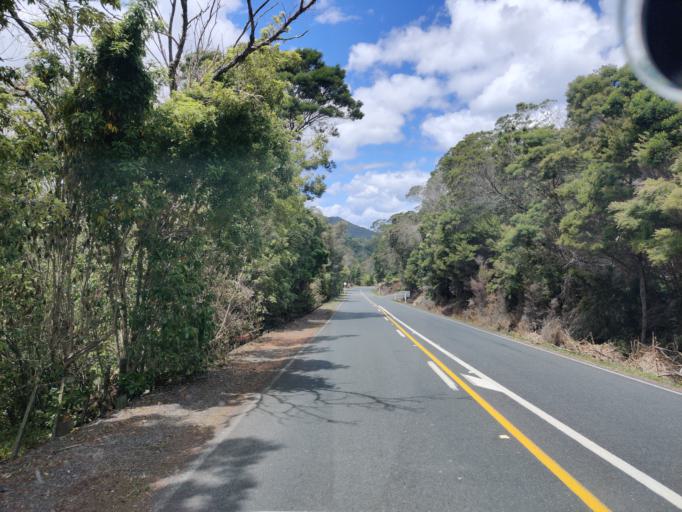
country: NZ
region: Northland
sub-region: Far North District
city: Paihia
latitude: -35.2683
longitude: 174.1337
